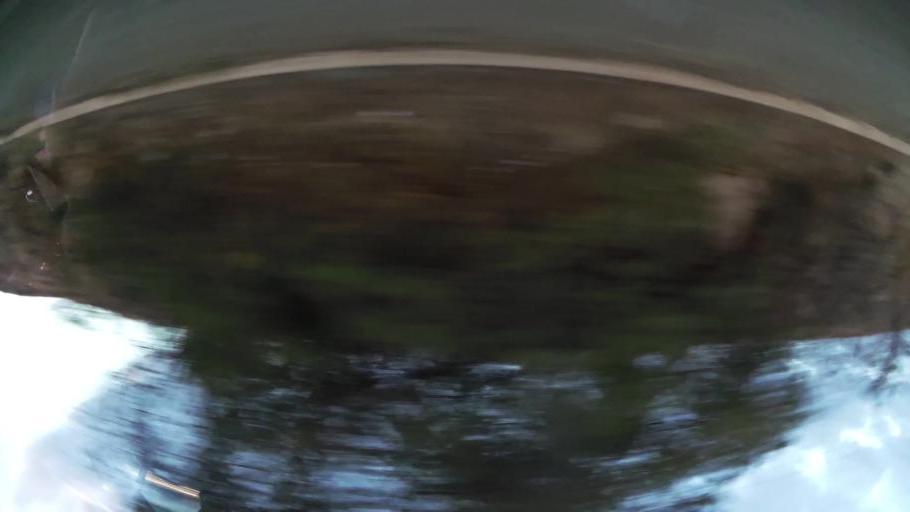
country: ZA
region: Gauteng
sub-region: West Rand District Municipality
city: Krugersdorp
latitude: -26.0378
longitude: 27.7227
